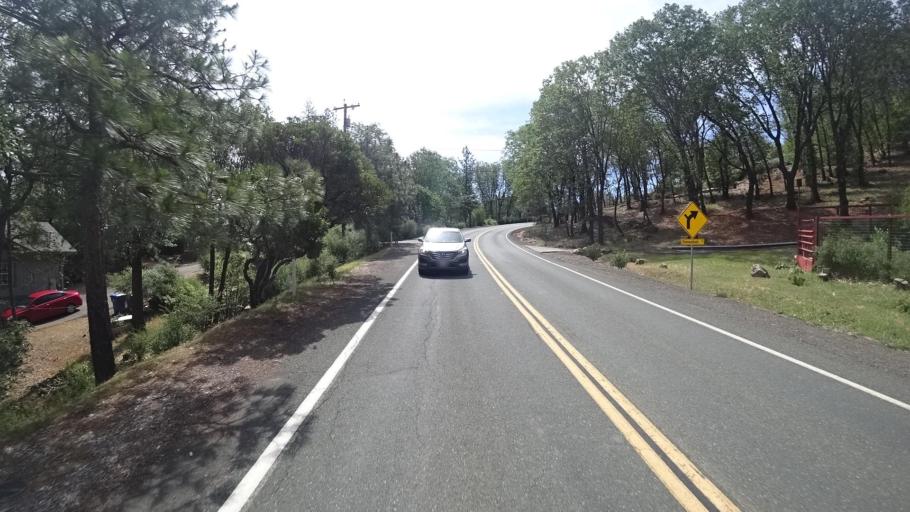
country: US
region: California
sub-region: Lake County
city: Cobb
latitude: 38.8687
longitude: -122.6873
